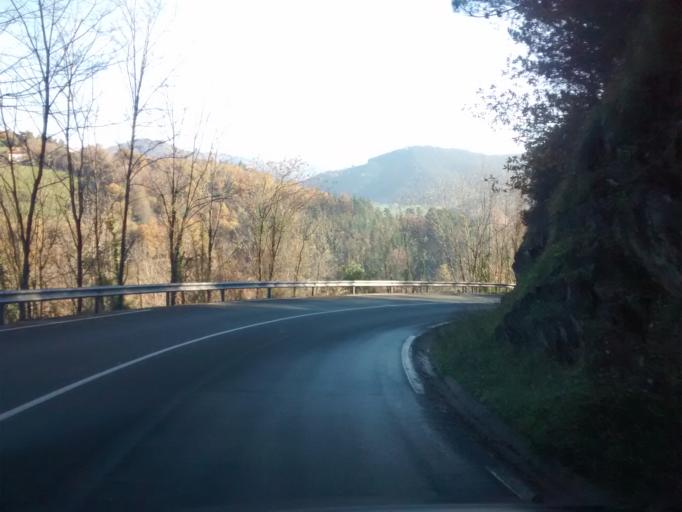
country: ES
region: Basque Country
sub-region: Provincia de Guipuzcoa
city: Eibar
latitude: 43.1929
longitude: -2.4707
